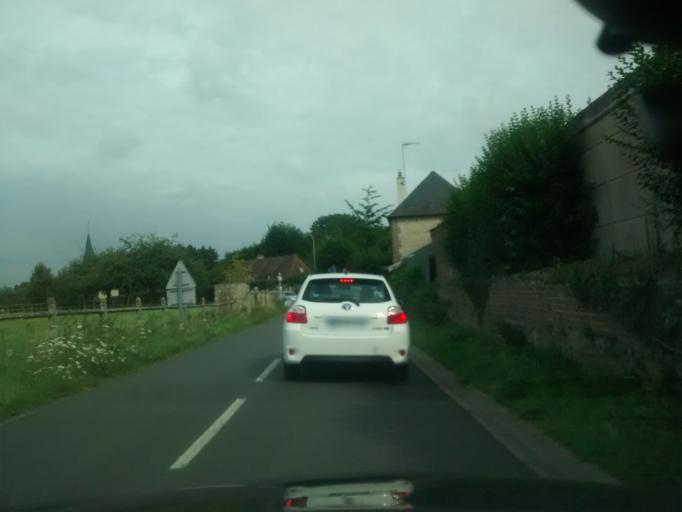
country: FR
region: Lower Normandy
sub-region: Departement du Calvados
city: Deauville
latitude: 49.3230
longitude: 0.0623
